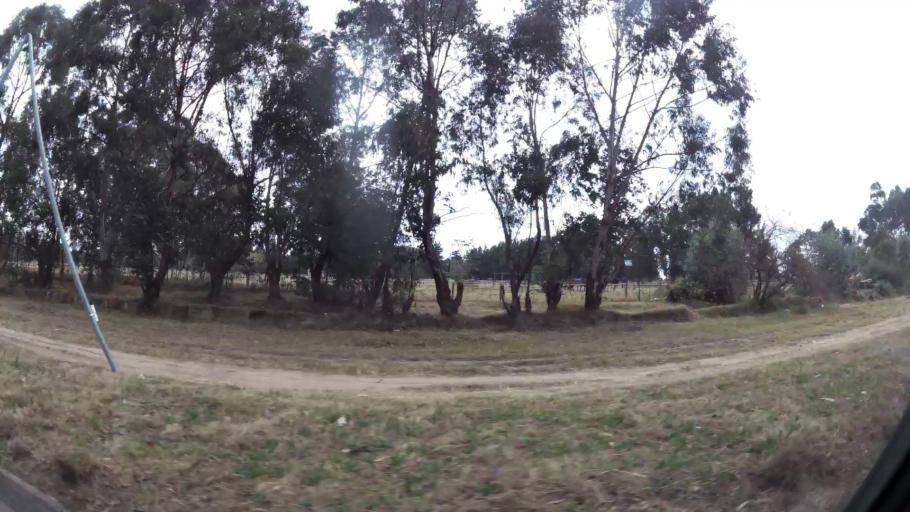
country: ZA
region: Gauteng
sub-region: West Rand District Municipality
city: Muldersdriseloop
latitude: -26.0625
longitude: 27.8998
